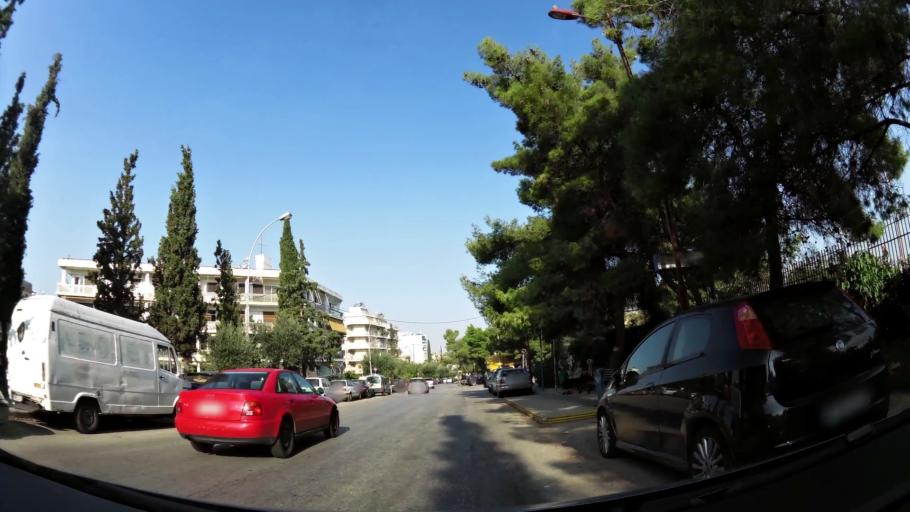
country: GR
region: Attica
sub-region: Nomos Attikis
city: Zografos
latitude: 37.9756
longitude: 23.7784
